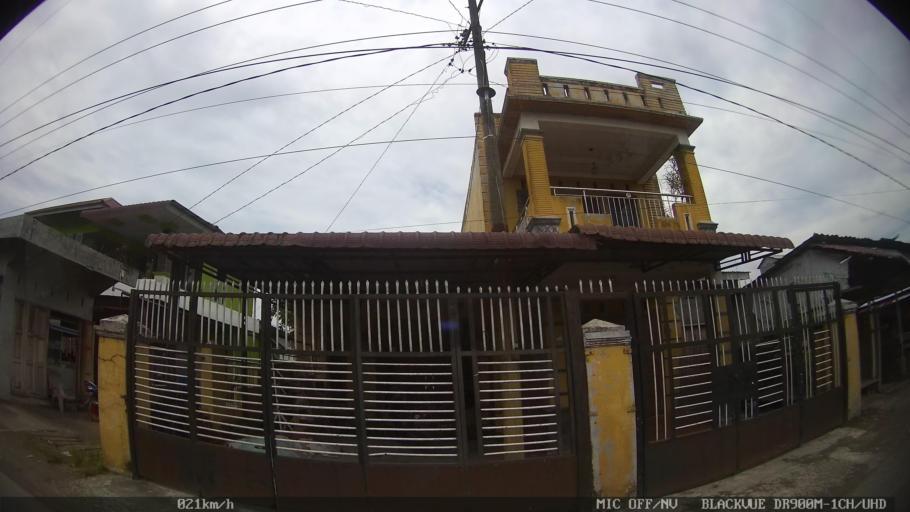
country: ID
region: North Sumatra
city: Binjai
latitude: 3.6354
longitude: 98.5535
